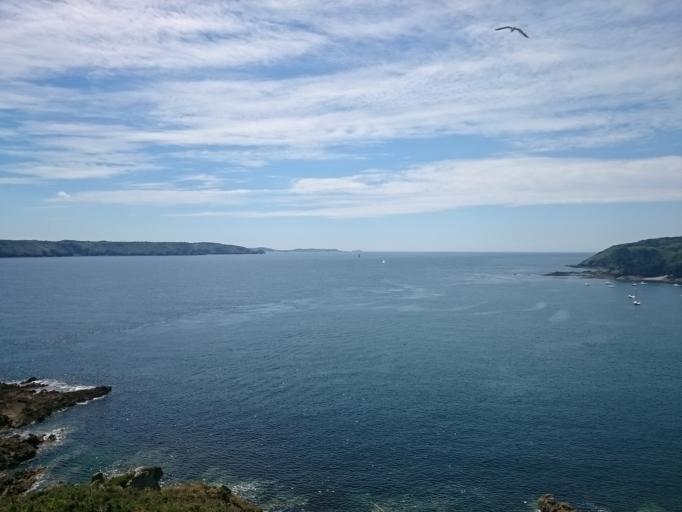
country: FR
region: Brittany
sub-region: Departement du Finistere
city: Roscanvel
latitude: 48.3553
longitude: -4.5589
